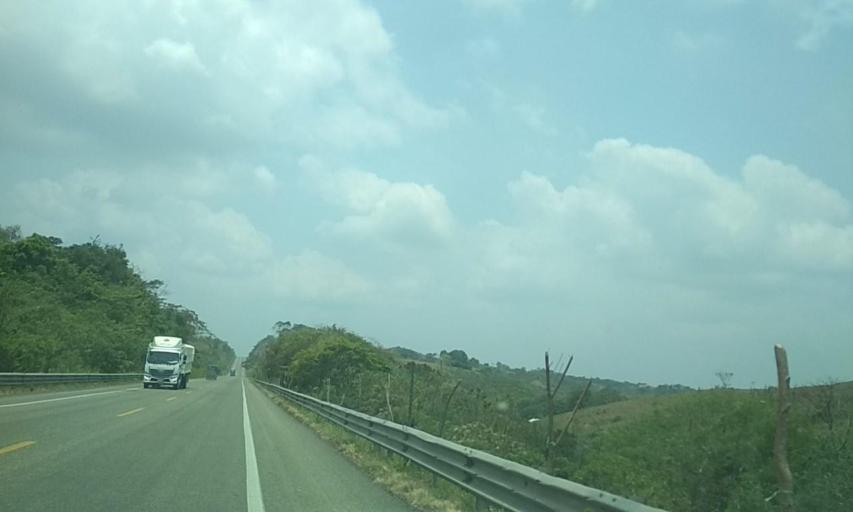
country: MX
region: Tabasco
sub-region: Huimanguillo
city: Francisco Rueda
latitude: 17.6524
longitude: -93.8402
